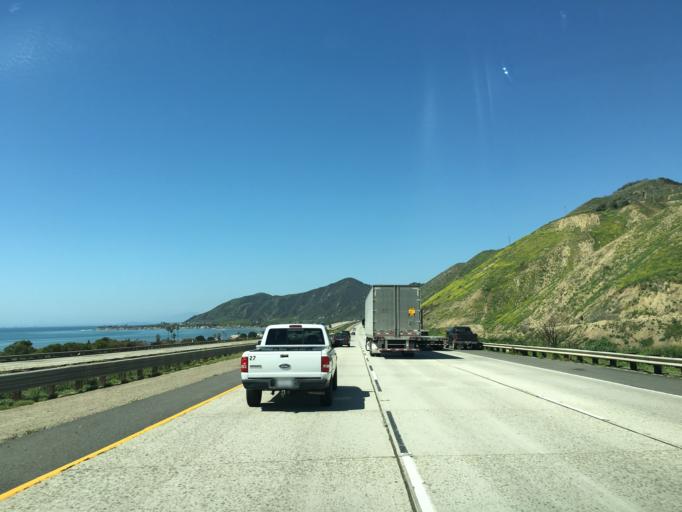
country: US
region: California
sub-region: Ventura County
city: Ventura
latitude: 34.3099
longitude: -119.3535
